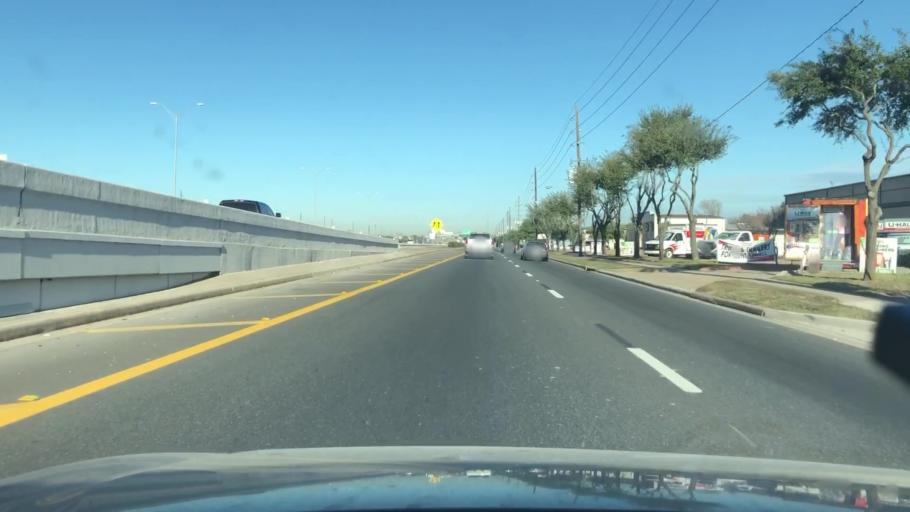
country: US
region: Texas
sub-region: Fort Bend County
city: Missouri City
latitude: 29.6471
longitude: -95.5421
